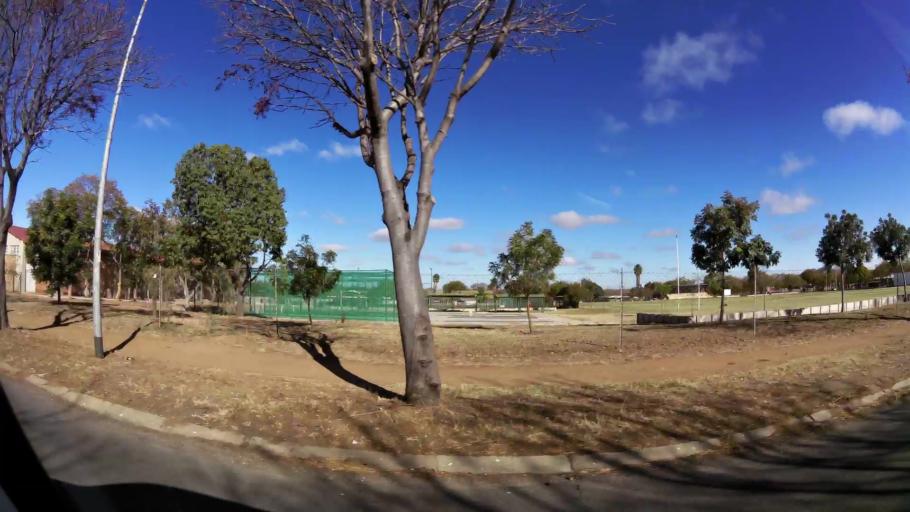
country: ZA
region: Limpopo
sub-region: Capricorn District Municipality
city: Polokwane
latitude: -23.8983
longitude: 29.4573
